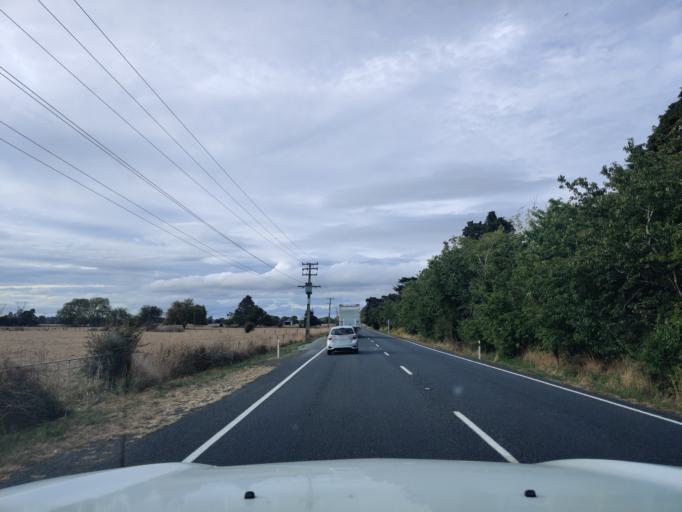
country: NZ
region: Waikato
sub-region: Hamilton City
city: Hamilton
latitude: -37.6935
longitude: 175.3382
